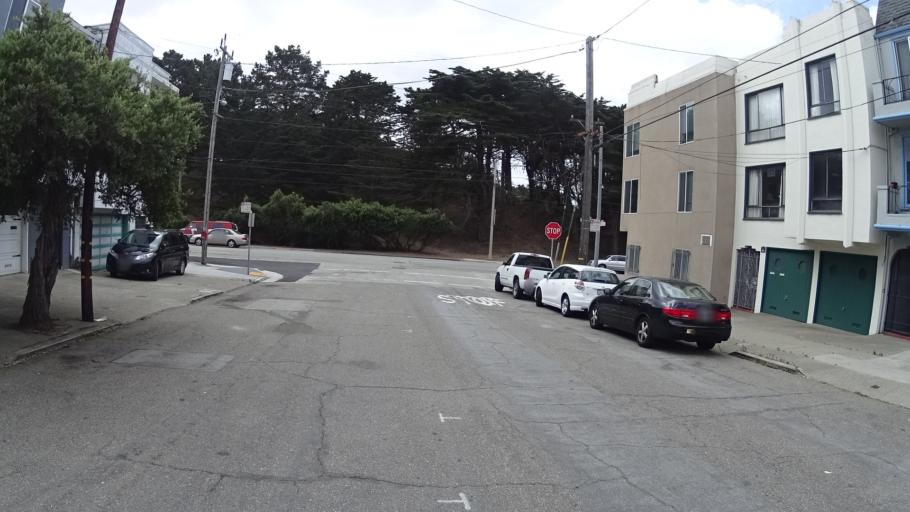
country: US
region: California
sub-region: San Mateo County
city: Daly City
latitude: 37.7719
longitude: -122.5057
